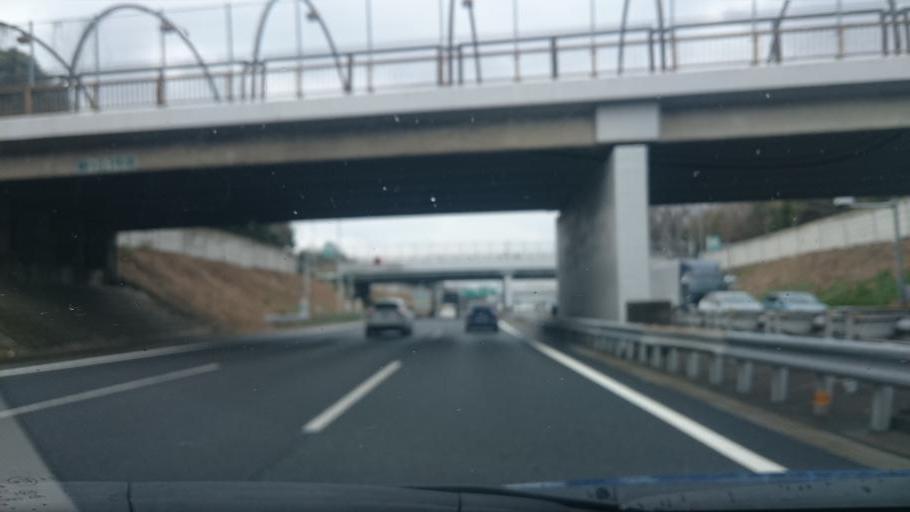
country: JP
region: Saitama
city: Sakado
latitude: 35.9233
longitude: 139.4129
